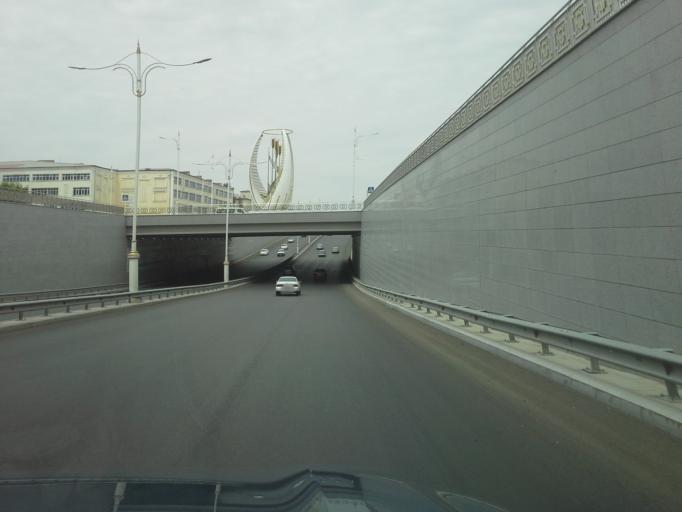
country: TM
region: Ahal
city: Ashgabat
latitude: 37.9324
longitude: 58.3941
